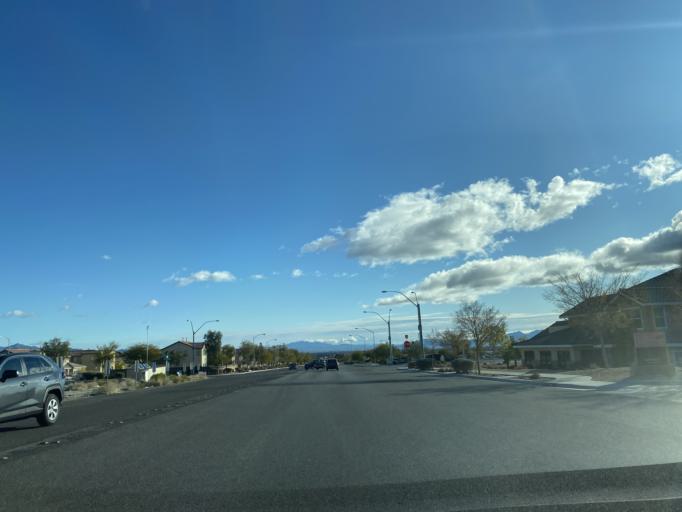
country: US
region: Nevada
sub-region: Clark County
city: Summerlin South
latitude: 36.2772
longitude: -115.2980
